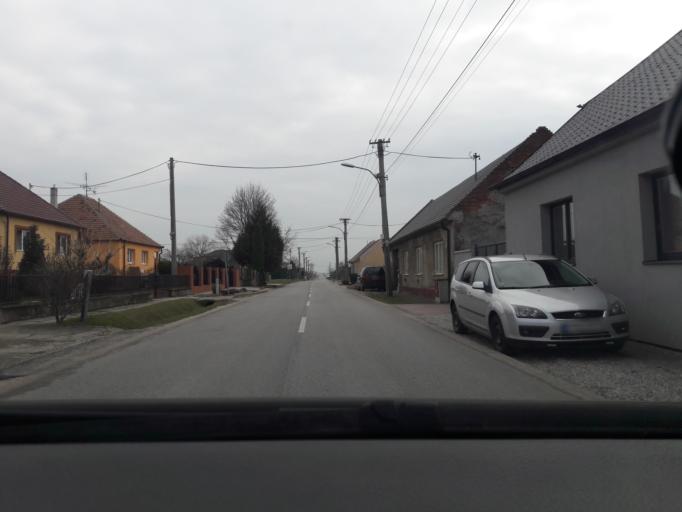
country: SK
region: Trnavsky
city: Smolenice
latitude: 48.4660
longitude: 17.4427
